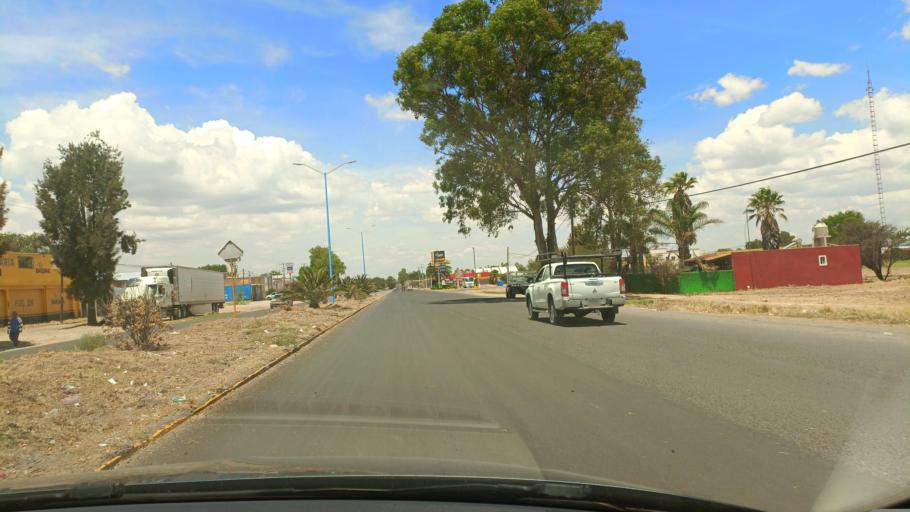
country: MX
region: Guanajuato
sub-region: San Luis de la Paz
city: San Ignacio
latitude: 21.2929
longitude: -100.5390
